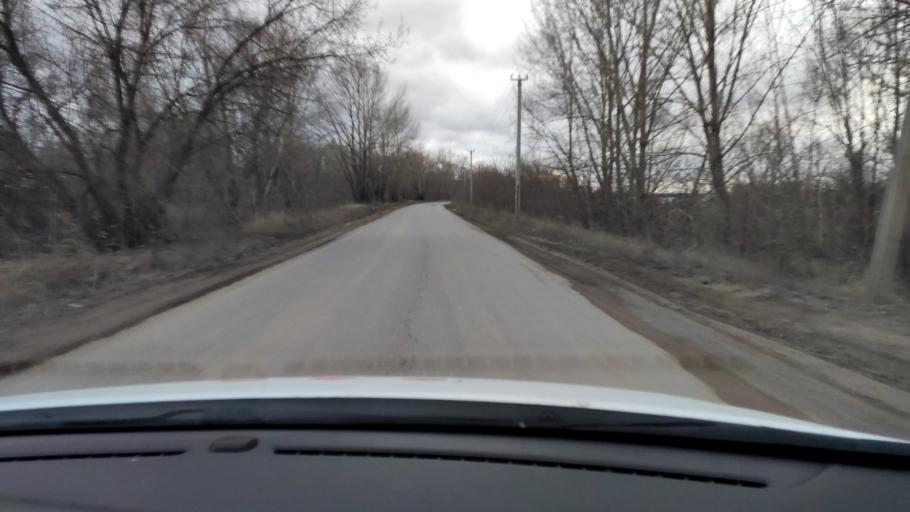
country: RU
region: Tatarstan
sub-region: Gorod Kazan'
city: Kazan
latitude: 55.7243
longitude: 49.0954
